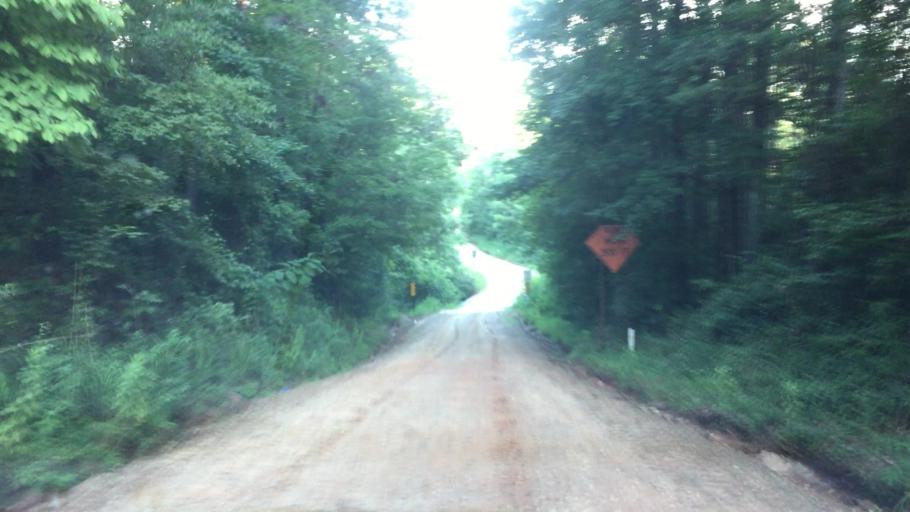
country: US
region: Georgia
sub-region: Henry County
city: McDonough
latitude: 33.5299
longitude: -84.1299
